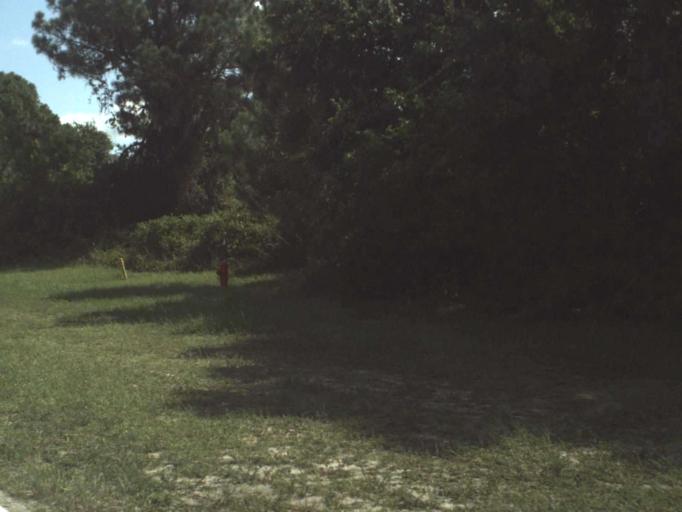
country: US
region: Florida
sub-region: Saint Lucie County
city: Port Saint Lucie
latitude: 27.2437
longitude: -80.3769
